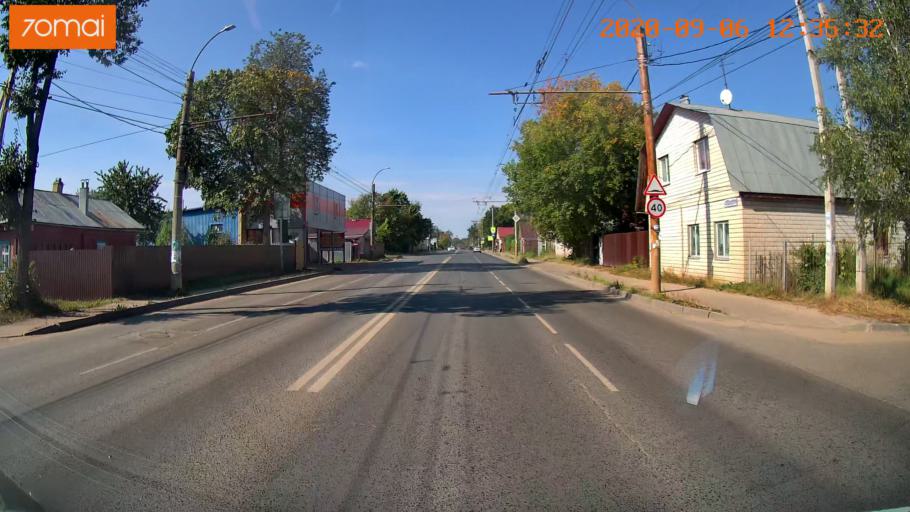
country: RU
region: Ivanovo
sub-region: Gorod Ivanovo
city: Ivanovo
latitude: 57.0201
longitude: 40.9926
